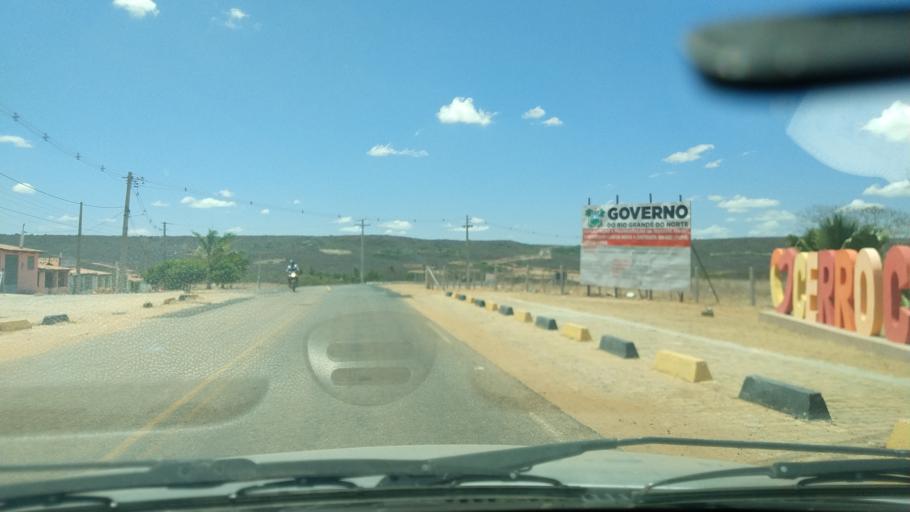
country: BR
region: Rio Grande do Norte
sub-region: Cerro Cora
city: Cerro Cora
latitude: -6.0563
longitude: -36.3598
